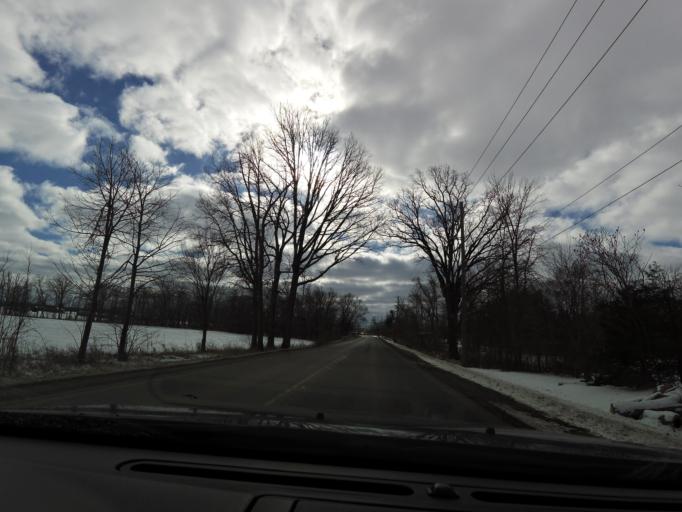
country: CA
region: Ontario
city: Hamilton
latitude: 43.1191
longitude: -79.6566
